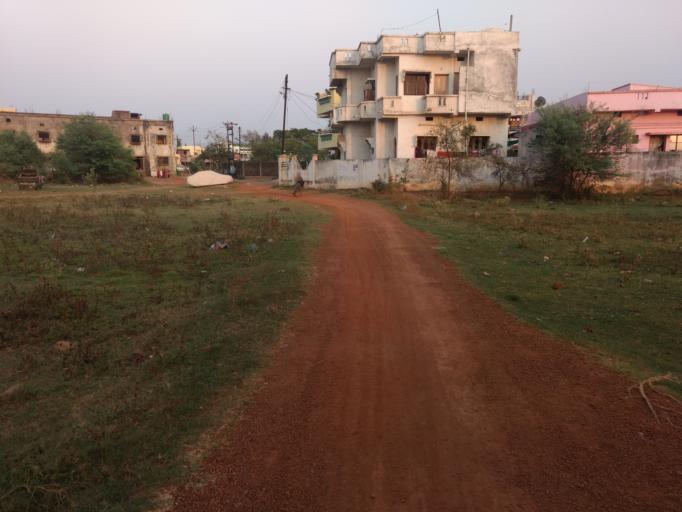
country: IN
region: Maharashtra
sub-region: Bhandara
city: Pauni
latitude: 20.6123
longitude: 79.8545
